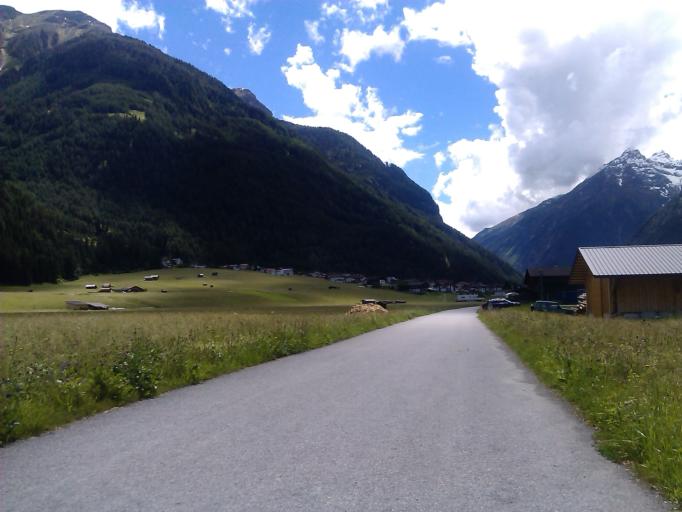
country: AT
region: Tyrol
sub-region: Politischer Bezirk Landeck
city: Pfunds
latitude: 46.9741
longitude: 10.5527
